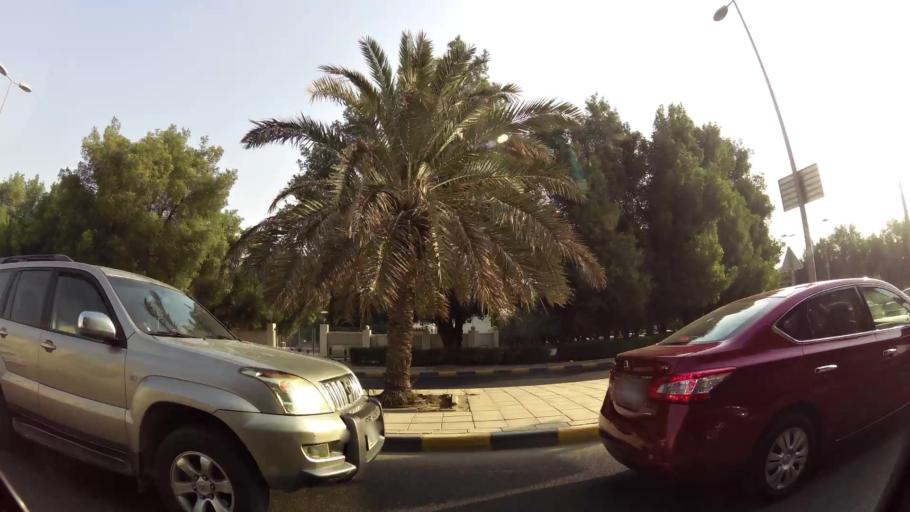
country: KW
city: Bayan
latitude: 29.3016
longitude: 48.0556
